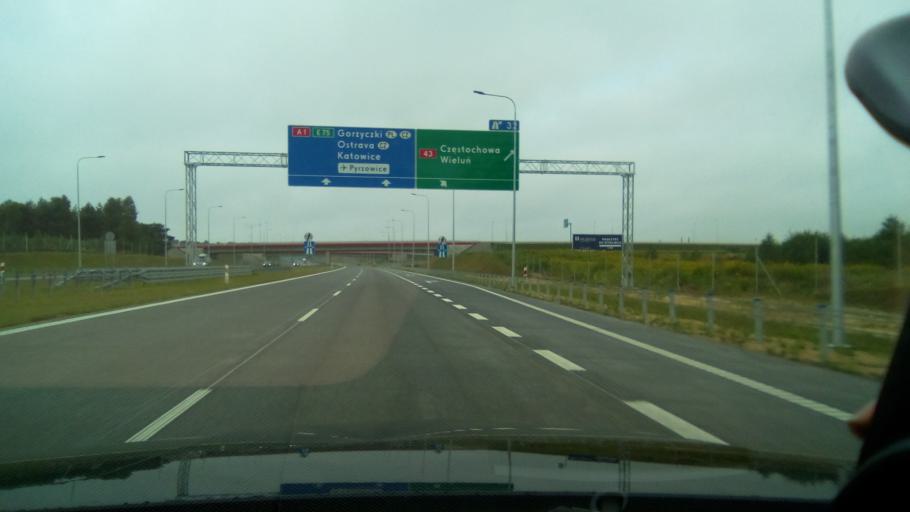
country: PL
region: Silesian Voivodeship
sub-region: Powiat klobucki
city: Kamyk
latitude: 50.8505
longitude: 19.0447
